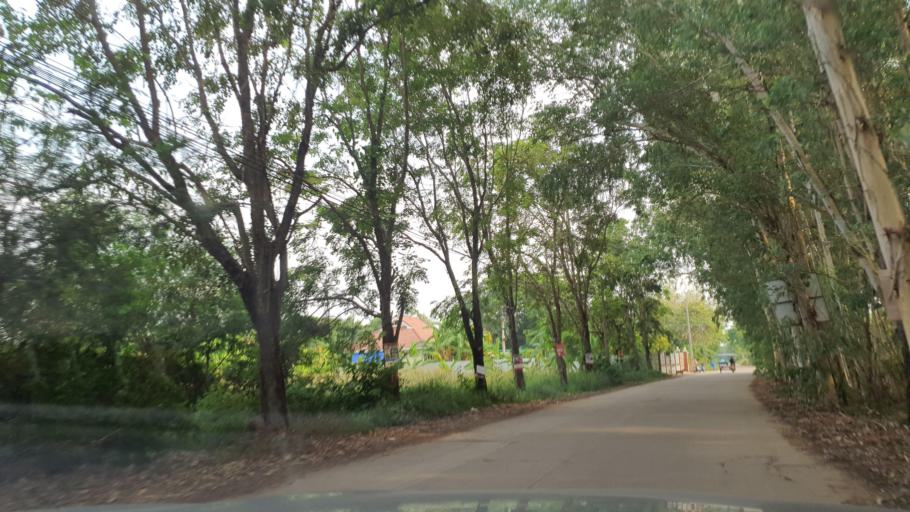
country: TH
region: Rayong
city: Rayong
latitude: 12.6169
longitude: 101.4018
